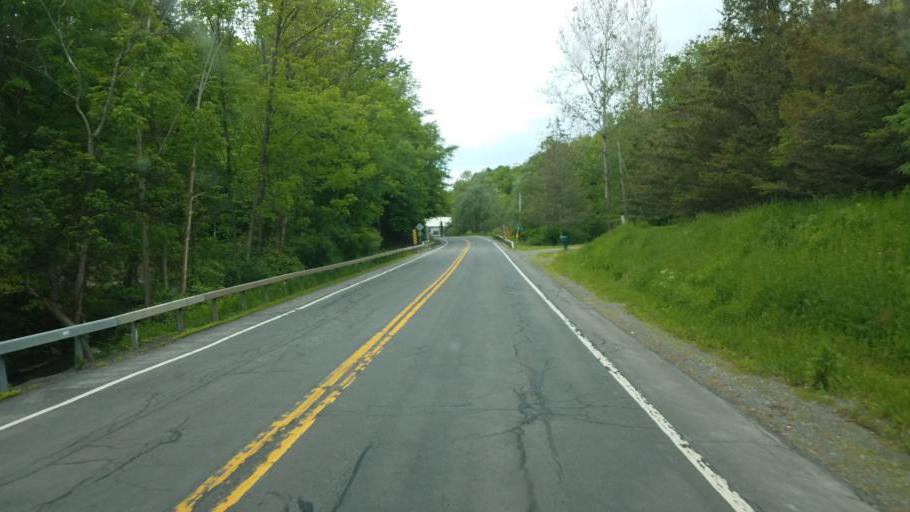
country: US
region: New York
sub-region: Herkimer County
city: Frankfort
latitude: 42.9699
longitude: -75.1006
